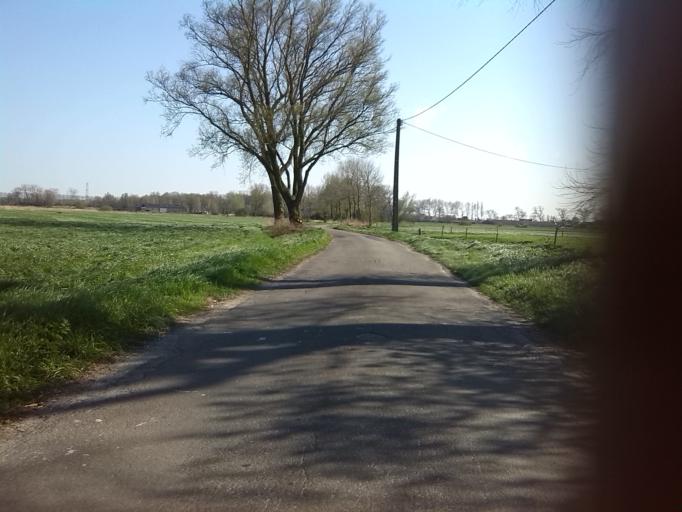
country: BE
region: Flanders
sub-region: Provincie West-Vlaanderen
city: Jabbeke
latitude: 51.2173
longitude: 3.1279
